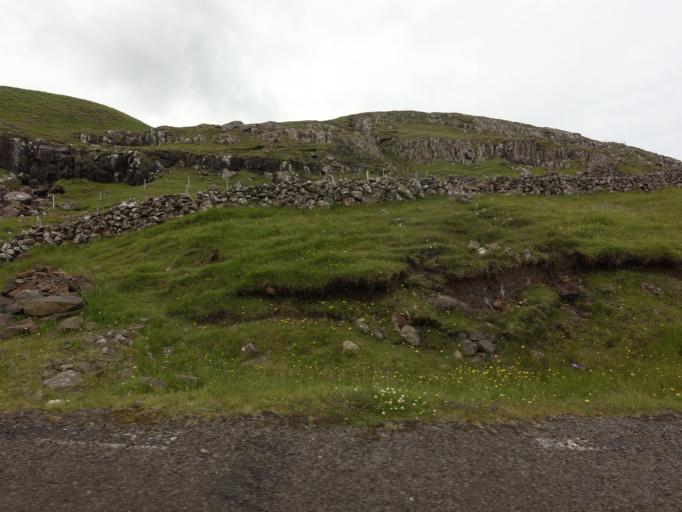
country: FO
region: Suduroy
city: Vagur
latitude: 61.4415
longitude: -6.7317
